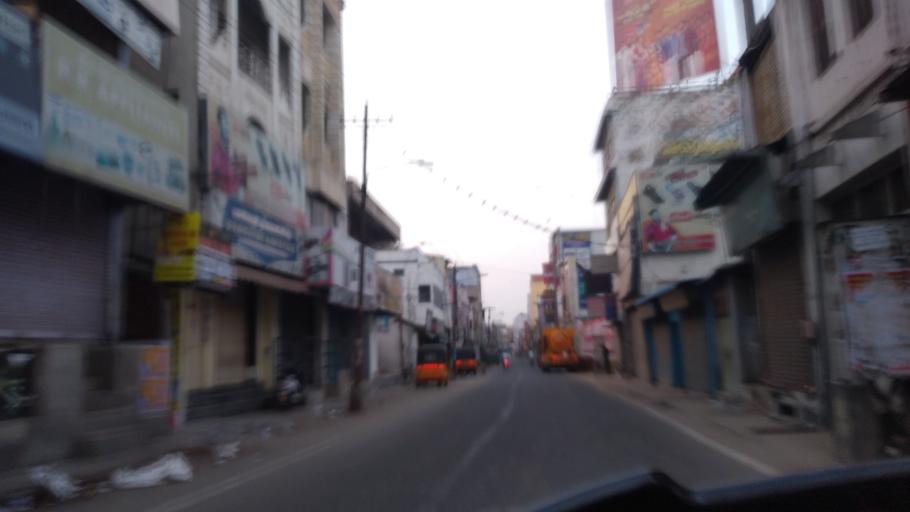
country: IN
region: Tamil Nadu
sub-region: Coimbatore
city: Coimbatore
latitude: 10.9974
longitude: 76.9601
